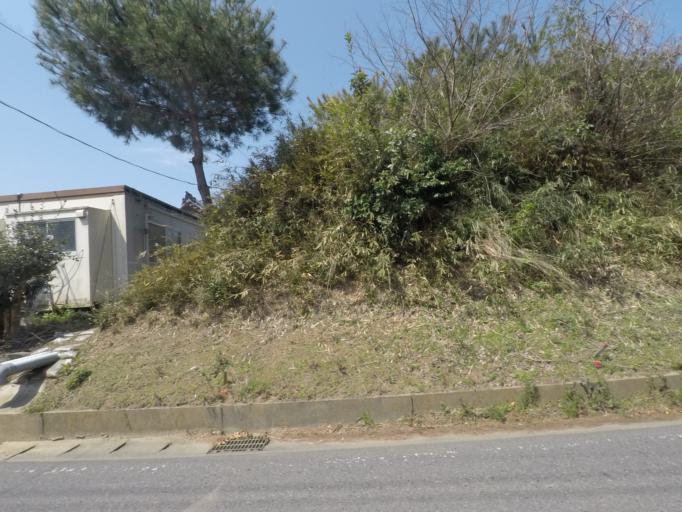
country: JP
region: Chiba
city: Naruto
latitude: 35.6961
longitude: 140.4293
